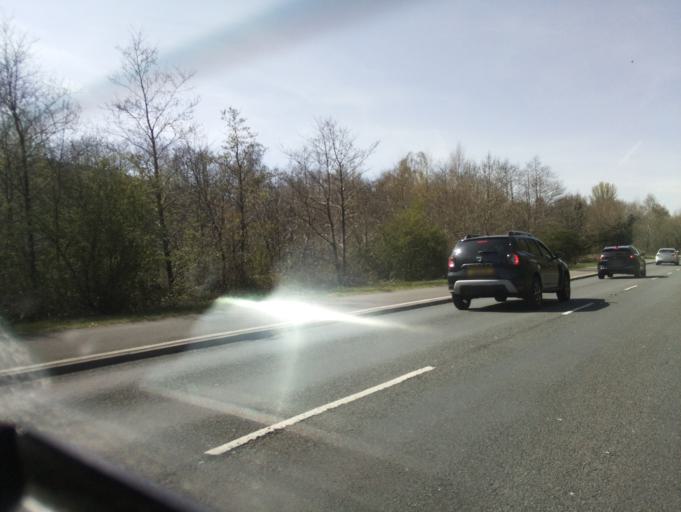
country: GB
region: Wales
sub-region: Rhondda Cynon Taf
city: Cwmbach
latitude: 51.6909
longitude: -3.3999
